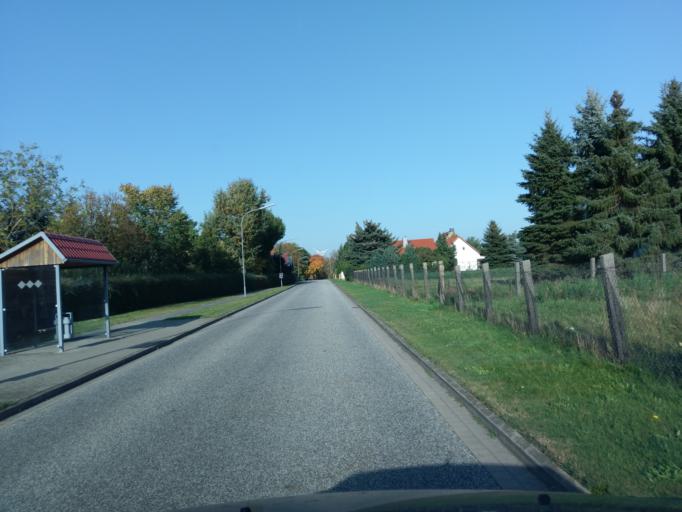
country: DE
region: Brandenburg
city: Muhlberg
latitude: 51.4486
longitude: 13.2323
